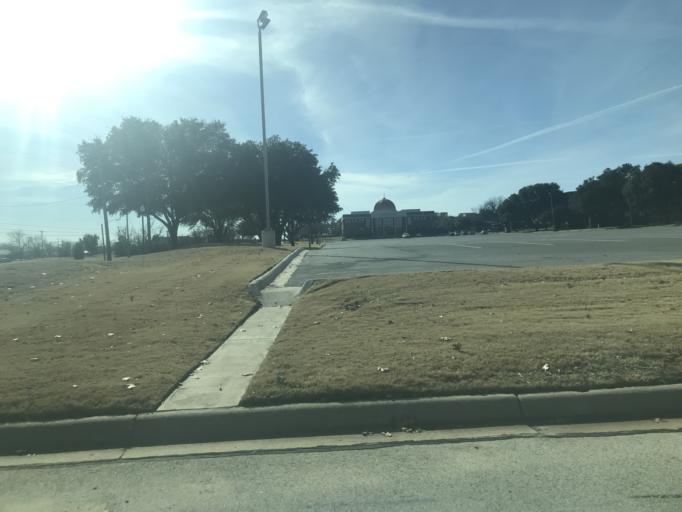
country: US
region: Texas
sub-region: Taylor County
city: Abilene
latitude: 32.4788
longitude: -99.7315
